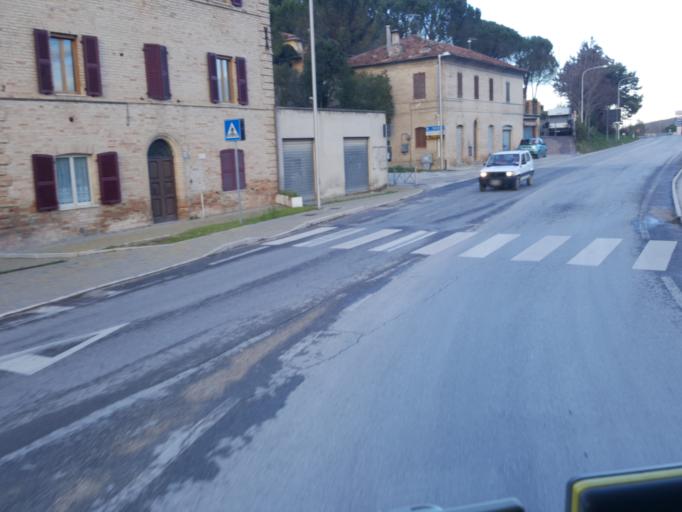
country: IT
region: The Marches
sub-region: Provincia di Macerata
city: San Severino Marche
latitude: 43.2412
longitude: 13.2192
